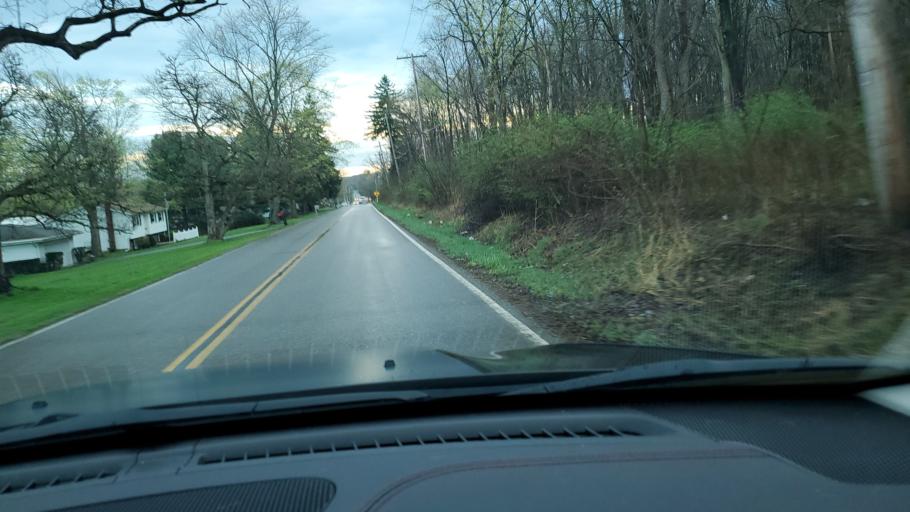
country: US
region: Ohio
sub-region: Trumbull County
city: Mineral Ridge
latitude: 41.1542
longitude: -80.7665
